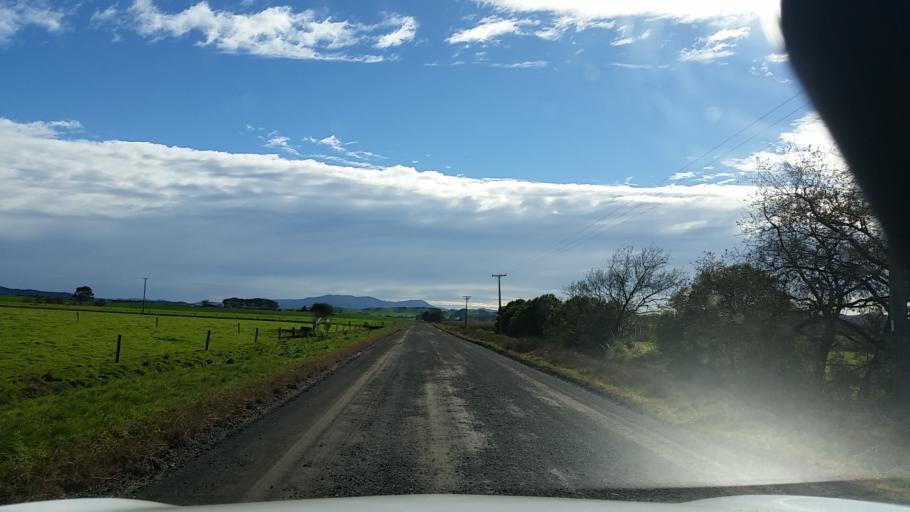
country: NZ
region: Waikato
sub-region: Hamilton City
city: Hamilton
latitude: -37.6348
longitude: 175.4295
